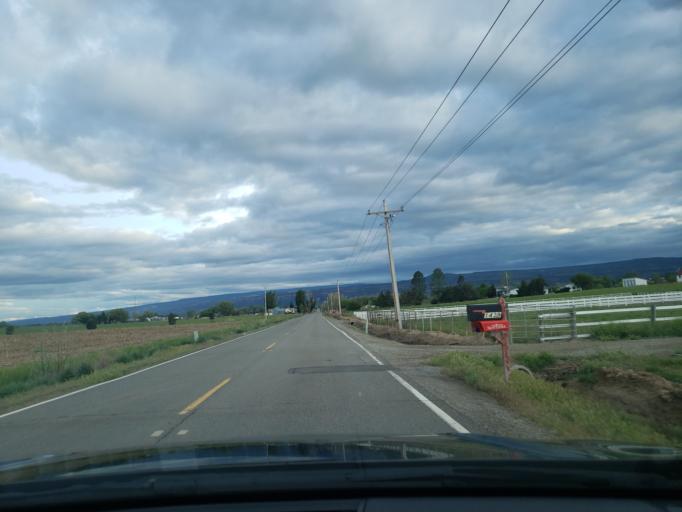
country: US
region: Colorado
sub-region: Mesa County
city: Fruita
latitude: 39.2134
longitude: -108.7011
